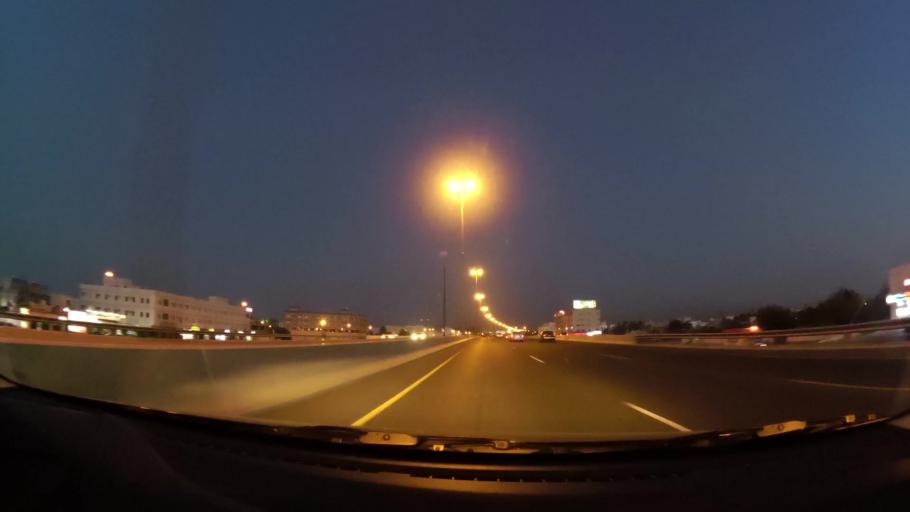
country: OM
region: Muhafazat Masqat
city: As Sib al Jadidah
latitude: 23.6291
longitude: 58.2339
